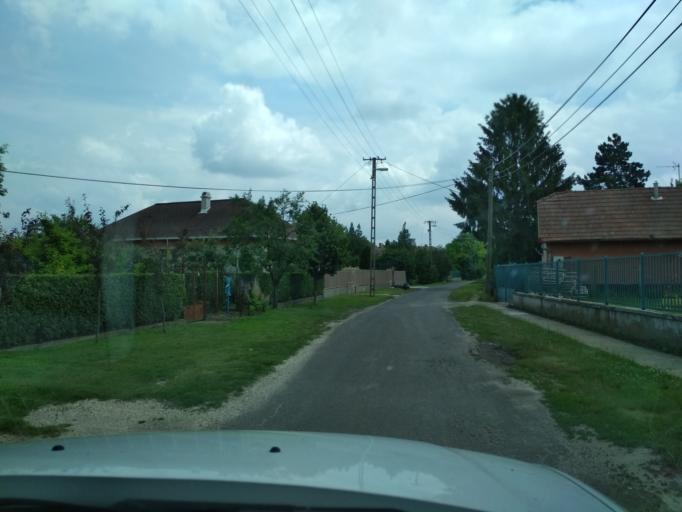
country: HU
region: Pest
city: Tapiobicske
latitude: 47.3627
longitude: 19.6770
